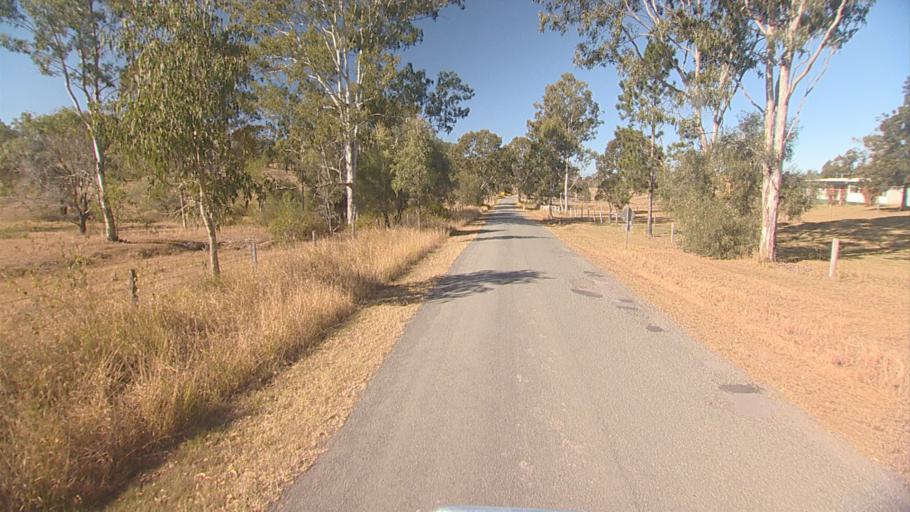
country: AU
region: Queensland
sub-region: Logan
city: Cedar Vale
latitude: -27.8486
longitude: 152.8931
